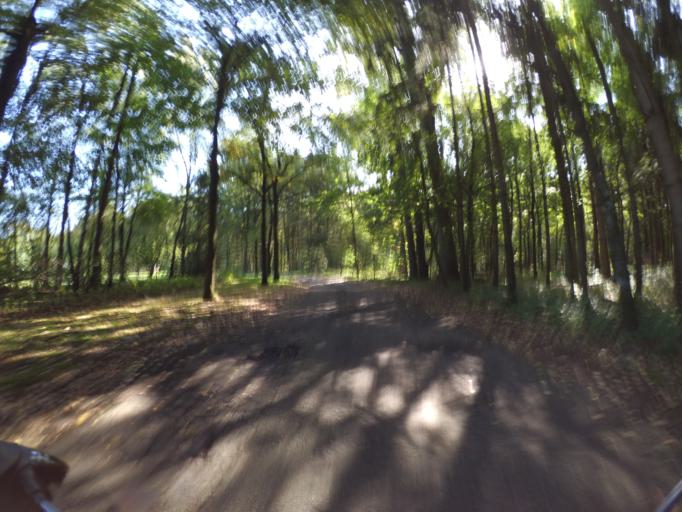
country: NL
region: Utrecht
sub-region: Gemeente Utrechtse Heuvelrug
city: Maarsbergen
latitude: 52.0389
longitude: 5.4214
